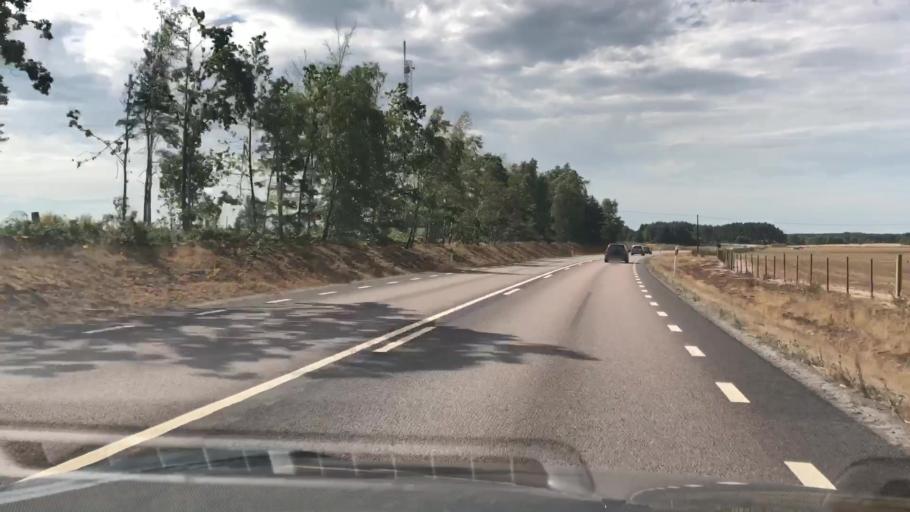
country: SE
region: Kalmar
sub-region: Torsas Kommun
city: Torsas
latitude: 56.3562
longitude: 16.0595
